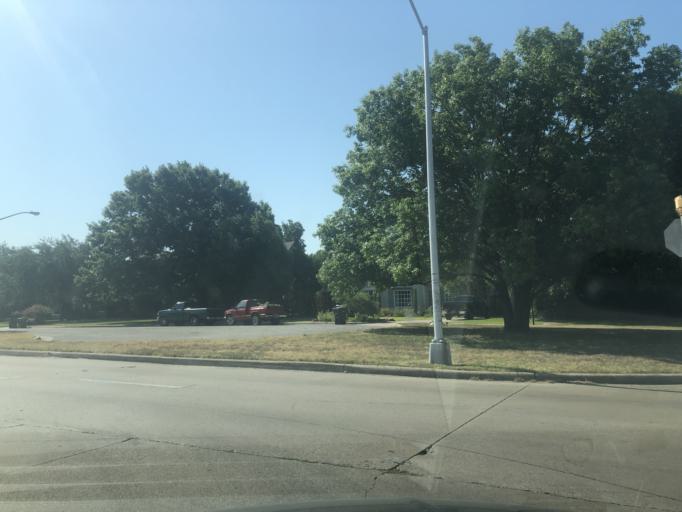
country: US
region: Texas
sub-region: Tarrant County
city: Edgecliff Village
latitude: 32.7019
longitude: -97.3746
